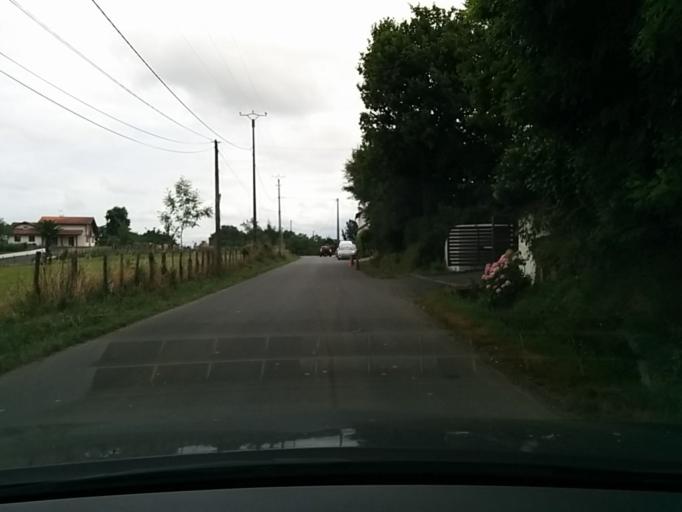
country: FR
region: Aquitaine
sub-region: Departement des Pyrenees-Atlantiques
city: Espelette
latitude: 43.3459
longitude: -1.4394
